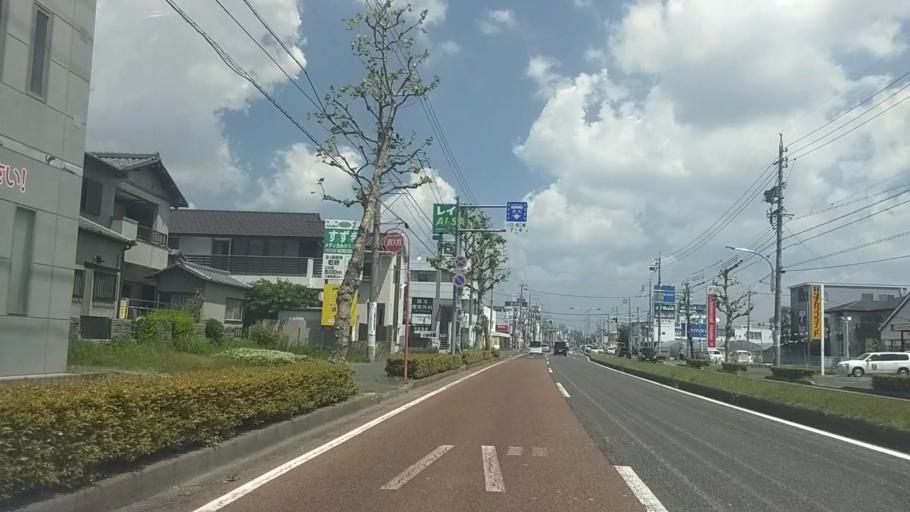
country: JP
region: Shizuoka
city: Hamamatsu
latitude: 34.7258
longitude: 137.7313
